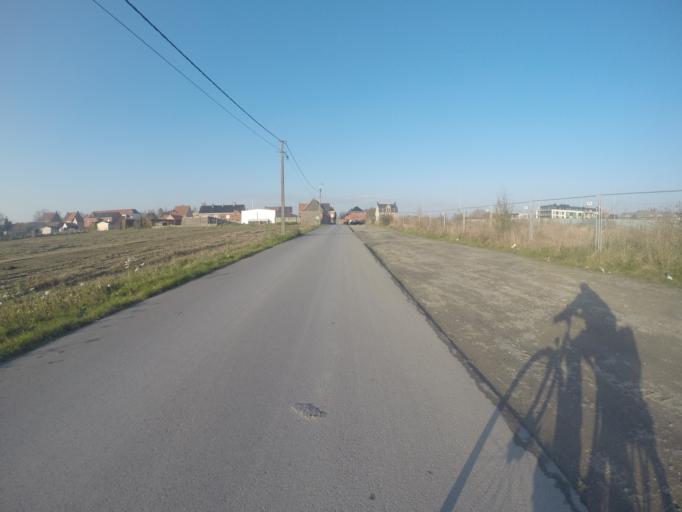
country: BE
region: Flanders
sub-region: Provincie Oost-Vlaanderen
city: Aalter
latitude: 51.0821
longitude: 3.4433
